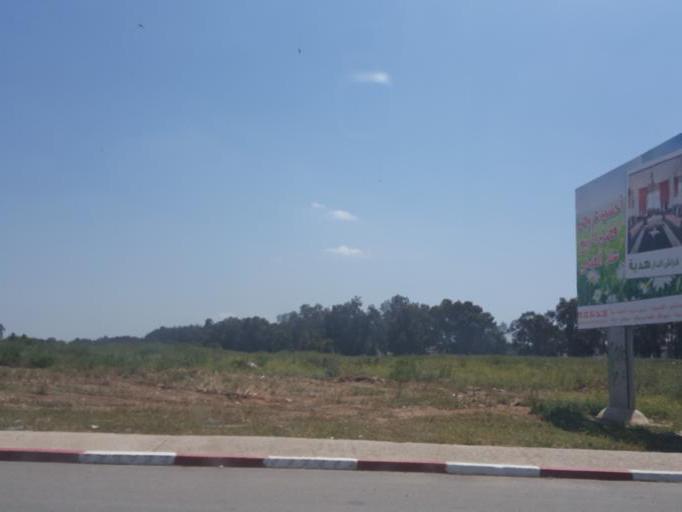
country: MA
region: Fes-Boulemane
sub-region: Fes
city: Fes
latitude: 34.0465
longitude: -5.0361
